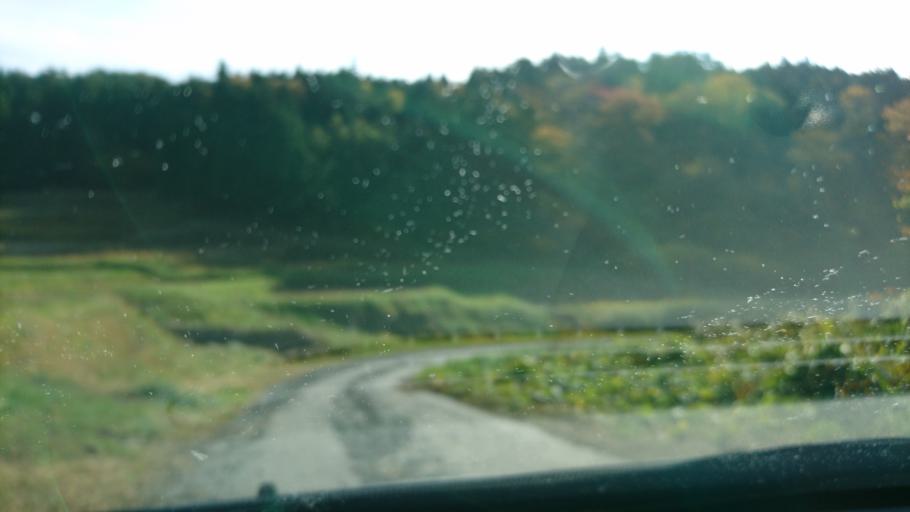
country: JP
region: Iwate
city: Ichinoseki
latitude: 38.9827
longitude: 141.1768
